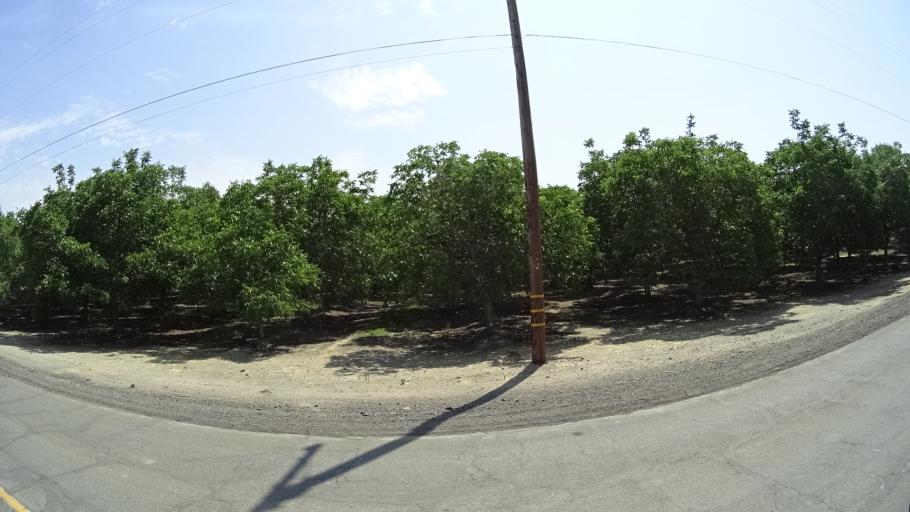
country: US
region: California
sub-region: Kings County
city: Armona
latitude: 36.3563
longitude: -119.7450
